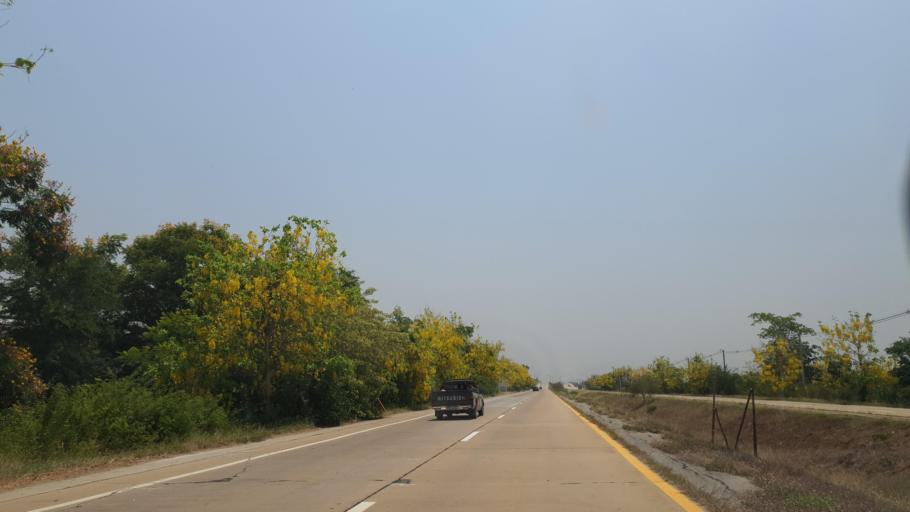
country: TH
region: Suphan Buri
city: Suphan Buri
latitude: 14.5454
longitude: 100.0771
